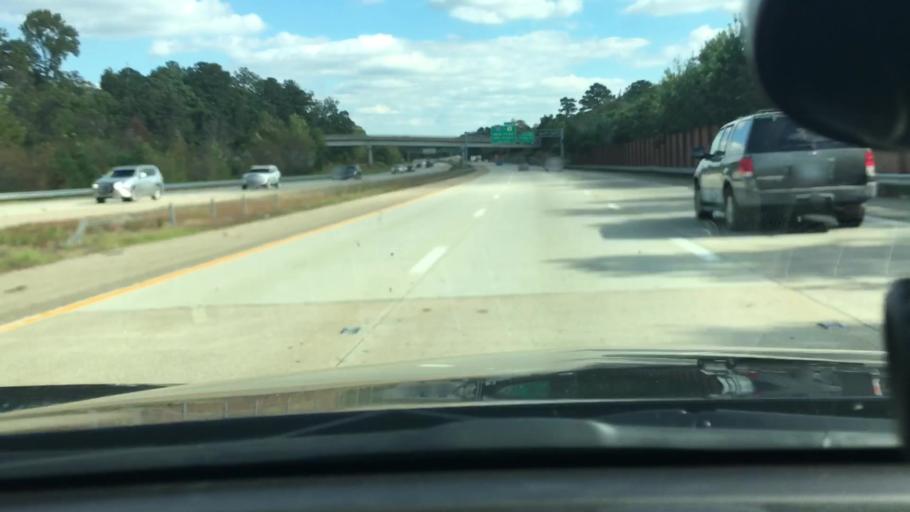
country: US
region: North Carolina
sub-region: Wake County
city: Knightdale
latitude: 35.7735
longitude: -78.5462
